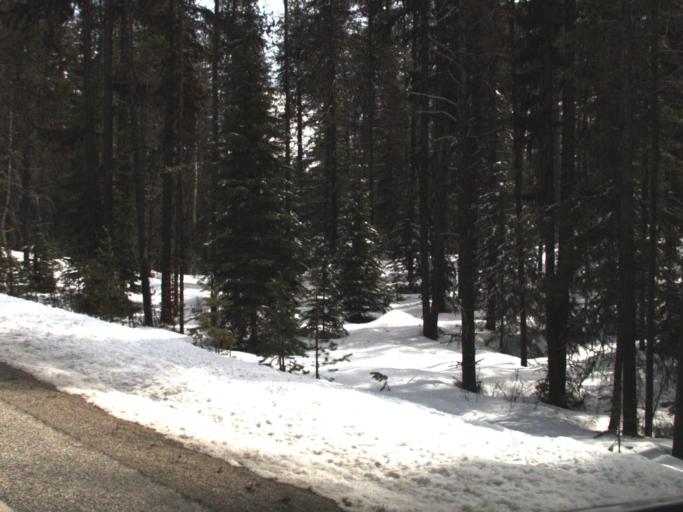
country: US
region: Washington
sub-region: Stevens County
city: Colville
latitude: 48.6572
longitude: -117.4783
